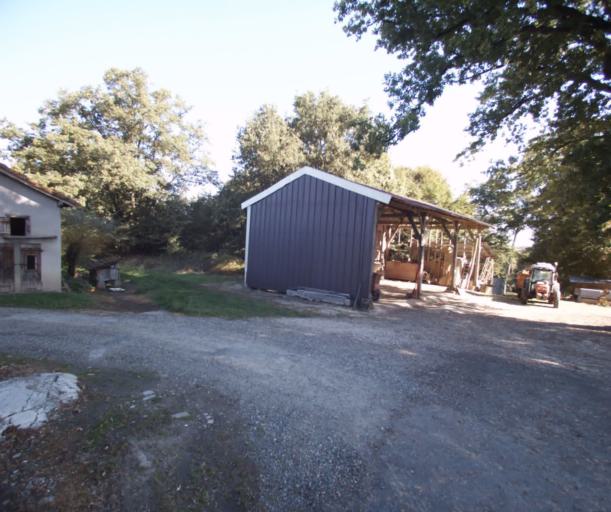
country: FR
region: Midi-Pyrenees
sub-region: Departement du Gers
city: Cazaubon
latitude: 43.9190
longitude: -0.0043
